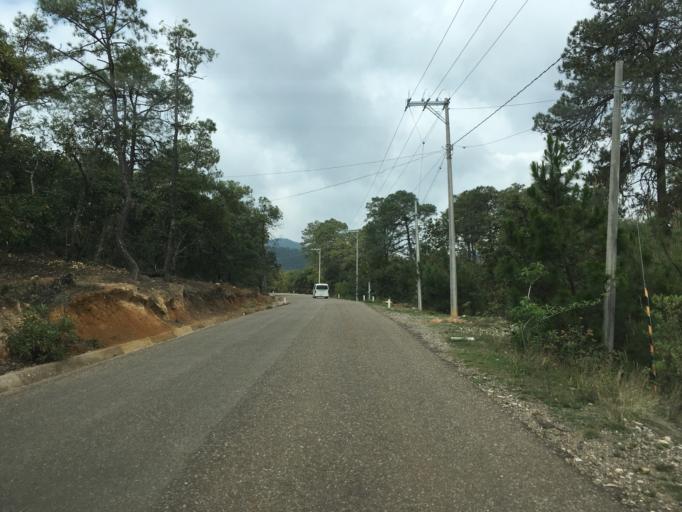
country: MX
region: Oaxaca
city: Santiago Tilantongo
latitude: 17.2152
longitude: -97.2803
